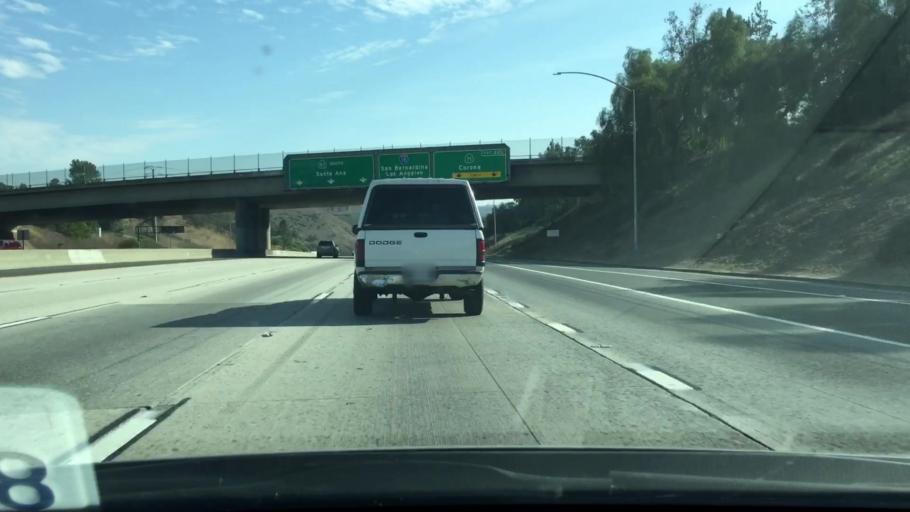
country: US
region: California
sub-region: Los Angeles County
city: San Dimas
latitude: 34.0784
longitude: -117.8150
